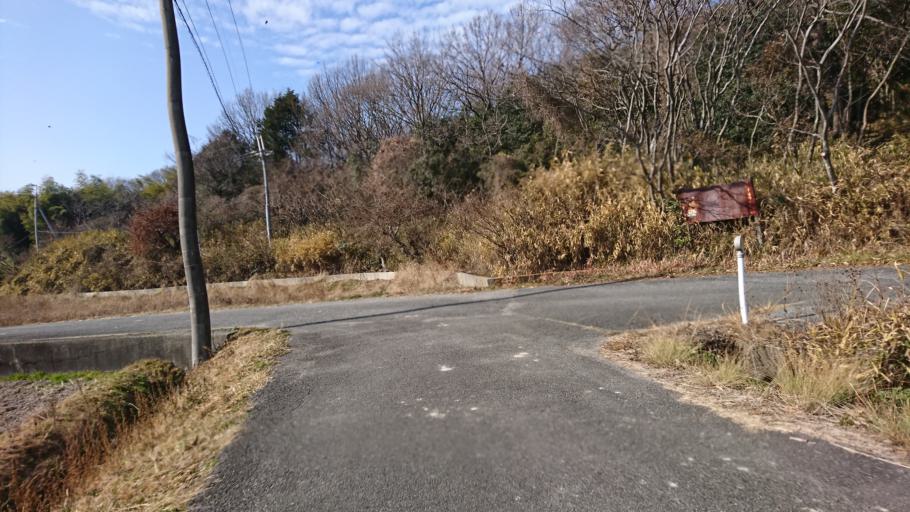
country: JP
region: Hyogo
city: Kakogawacho-honmachi
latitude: 34.8159
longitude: 134.8711
